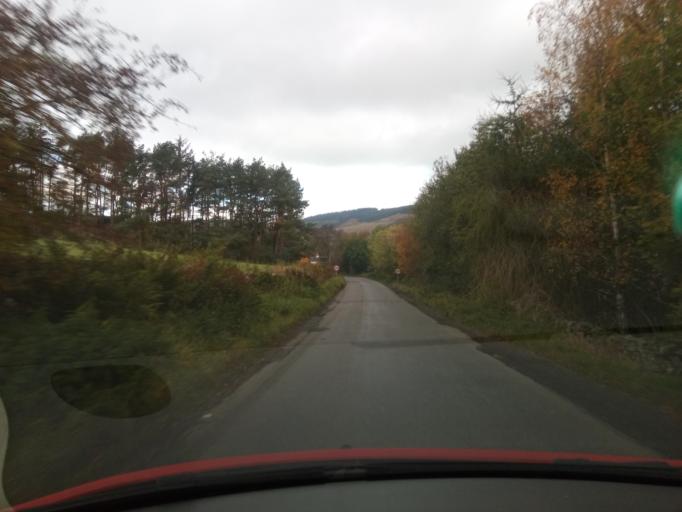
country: GB
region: Scotland
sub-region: The Scottish Borders
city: Innerleithen
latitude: 55.6377
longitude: -3.1087
